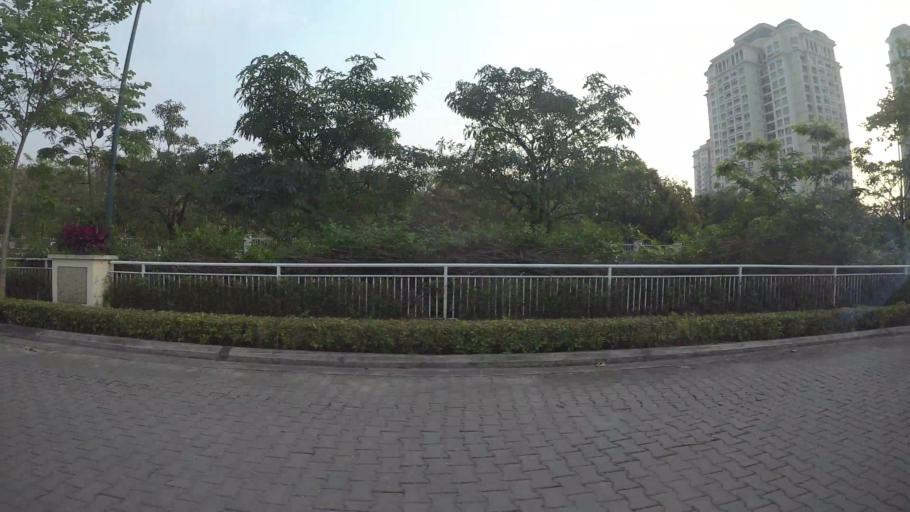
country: VN
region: Ha Noi
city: Tay Ho
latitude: 21.0790
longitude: 105.7947
